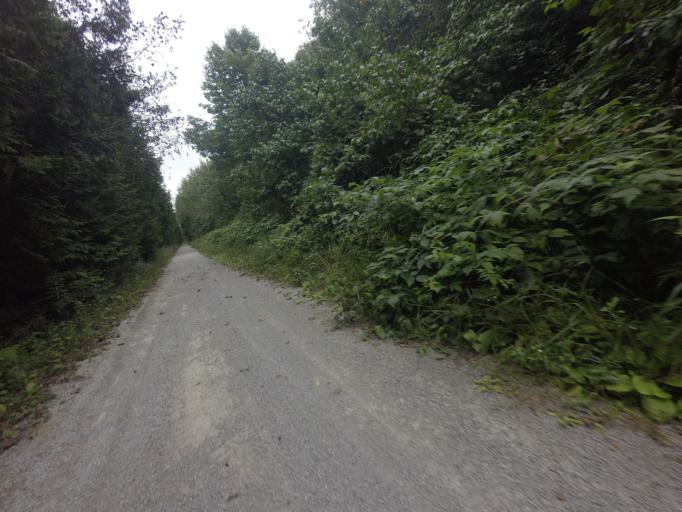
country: CA
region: Ontario
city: Uxbridge
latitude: 44.2856
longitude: -78.9975
